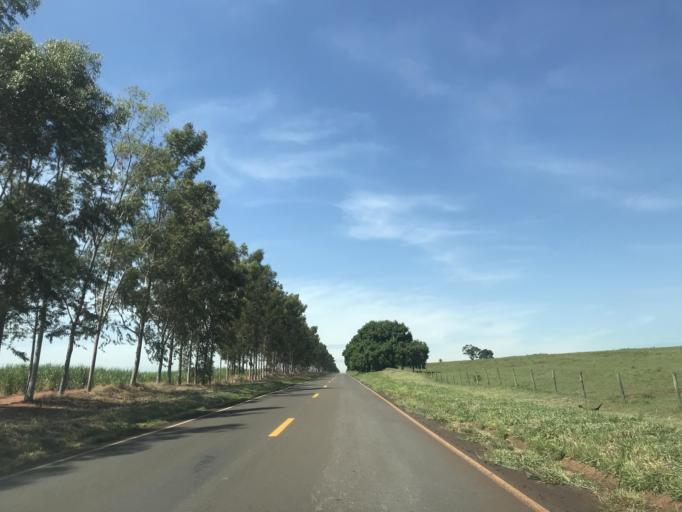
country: BR
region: Parana
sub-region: Paranavai
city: Nova Aurora
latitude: -22.8246
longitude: -52.6554
